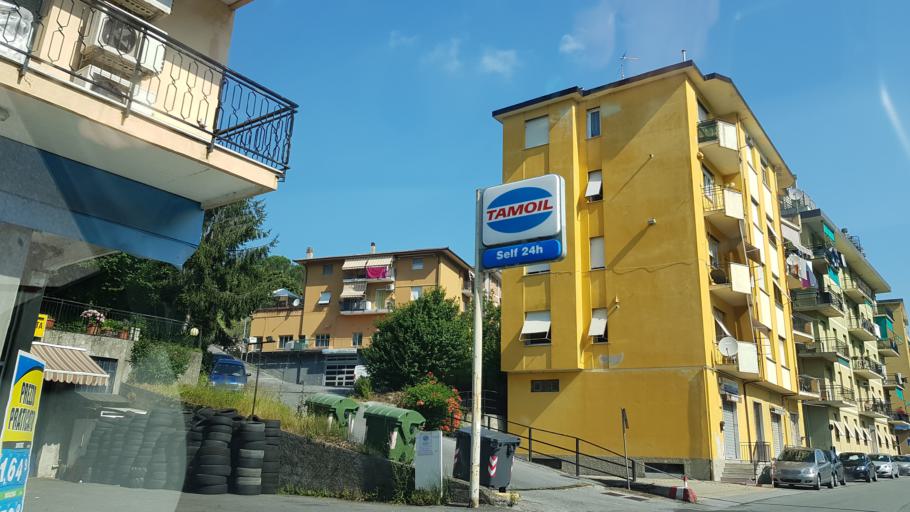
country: IT
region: Liguria
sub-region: Provincia di Genova
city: Pedemonte
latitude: 44.4944
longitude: 8.9204
